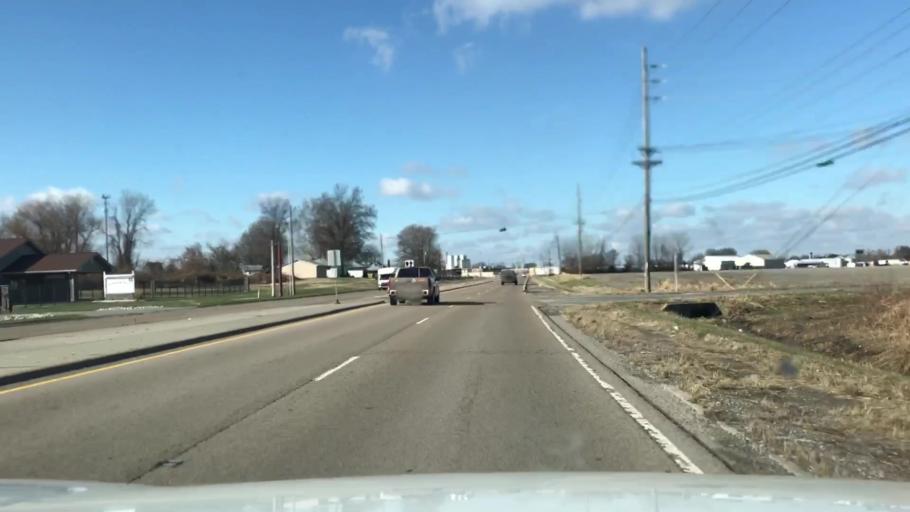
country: US
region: Illinois
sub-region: Saint Clair County
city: Washington Park
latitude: 38.6112
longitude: -90.0839
